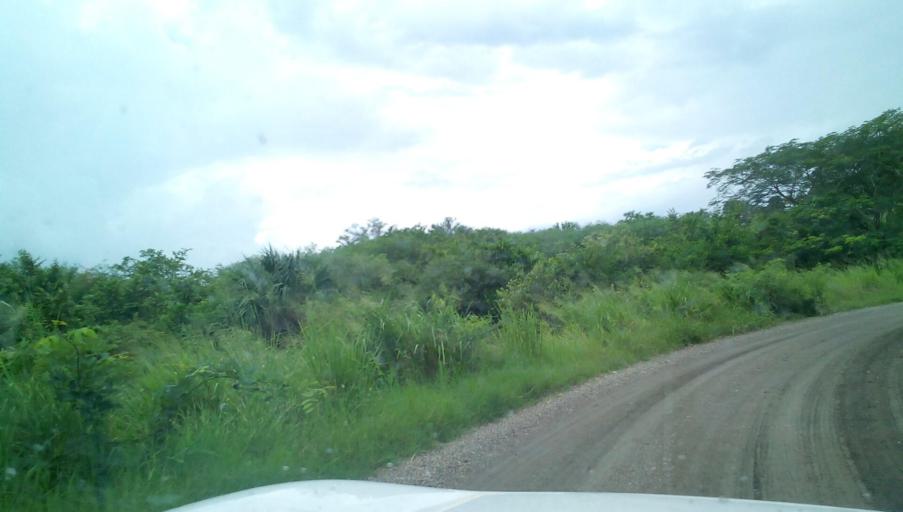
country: MX
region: Veracruz
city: Panuco
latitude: 21.8101
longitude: -98.1121
